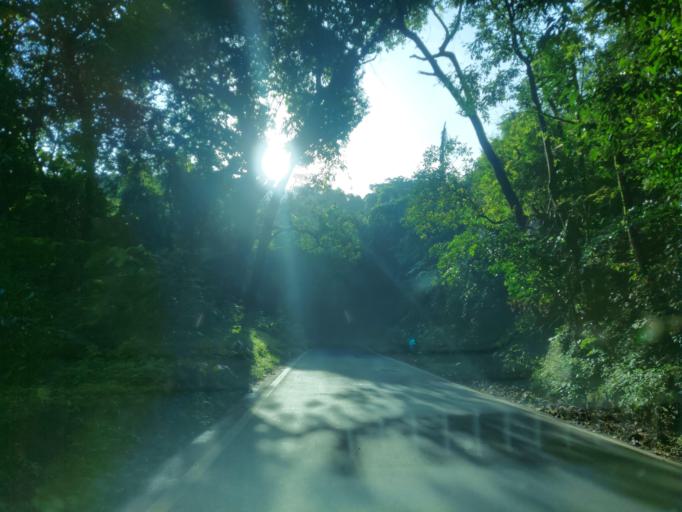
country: IN
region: Maharashtra
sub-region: Sindhudurg
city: Savantvadi
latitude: 15.9349
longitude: 73.9419
